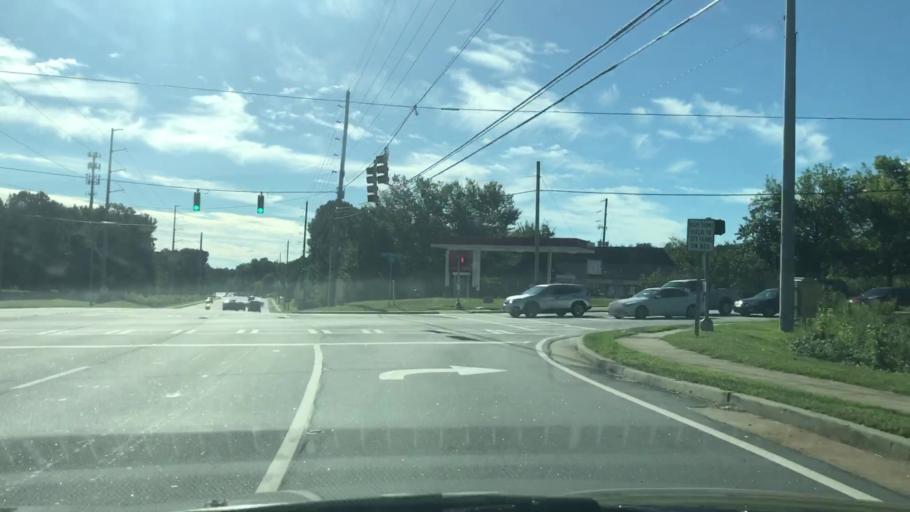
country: US
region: Georgia
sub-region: Gwinnett County
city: Mountain Park
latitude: 33.8085
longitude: -84.0967
